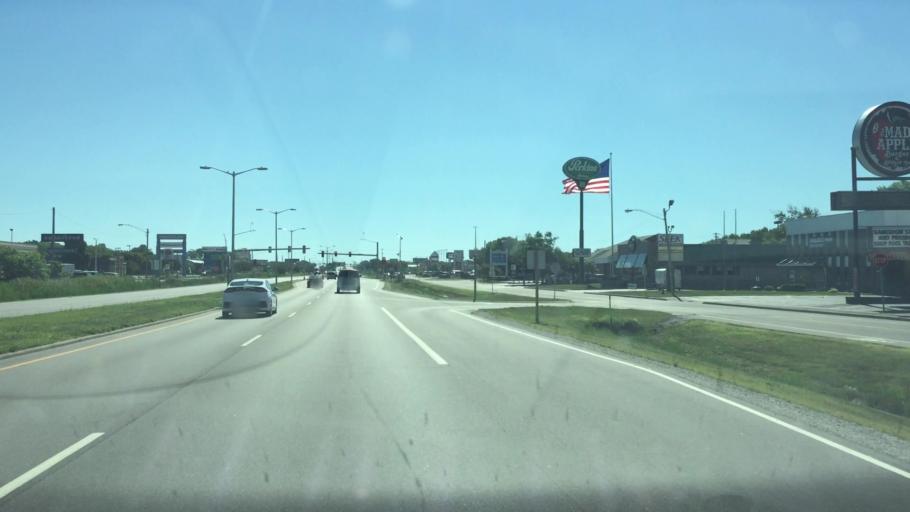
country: US
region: Wisconsin
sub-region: Outagamie County
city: Appleton
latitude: 44.2617
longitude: -88.4536
